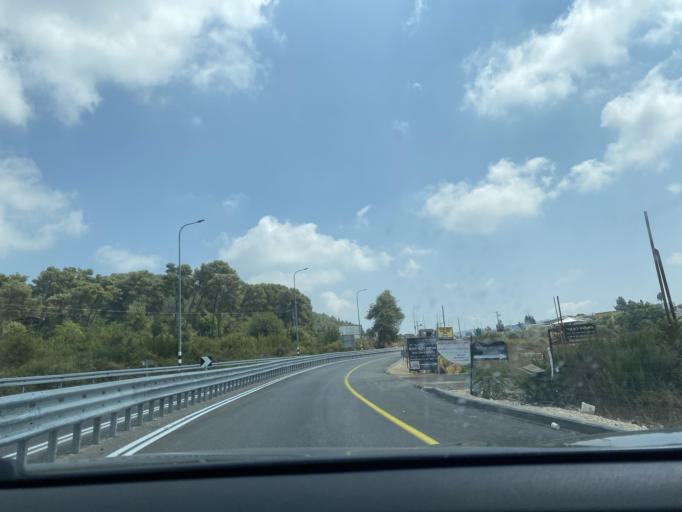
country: IL
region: Northern District
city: Kefar Weradim
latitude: 33.0046
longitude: 35.2962
